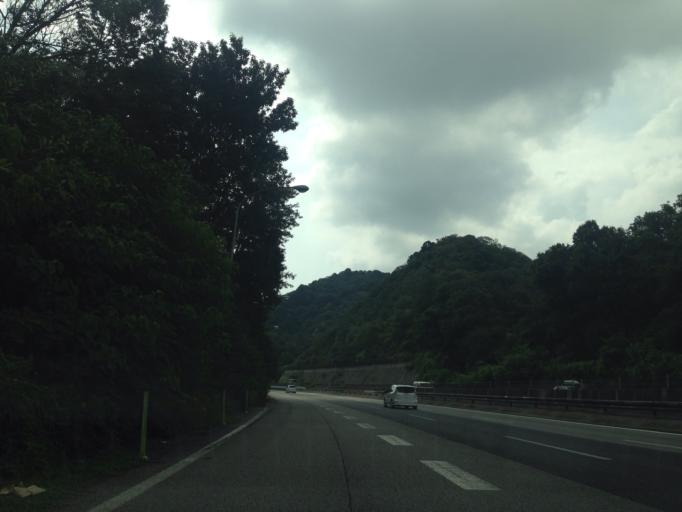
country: JP
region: Aichi
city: Okazaki
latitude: 34.9258
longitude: 137.2248
